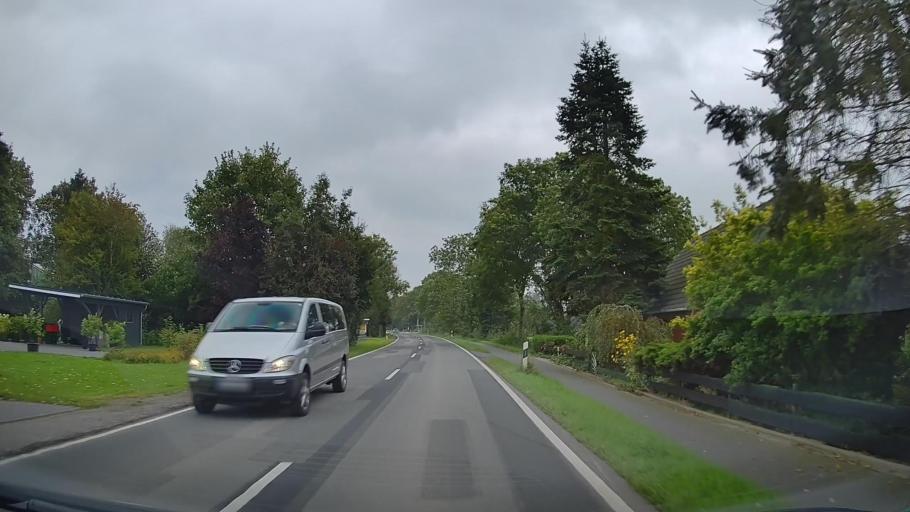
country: DE
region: Lower Saxony
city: Balje
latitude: 53.8120
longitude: 9.1173
